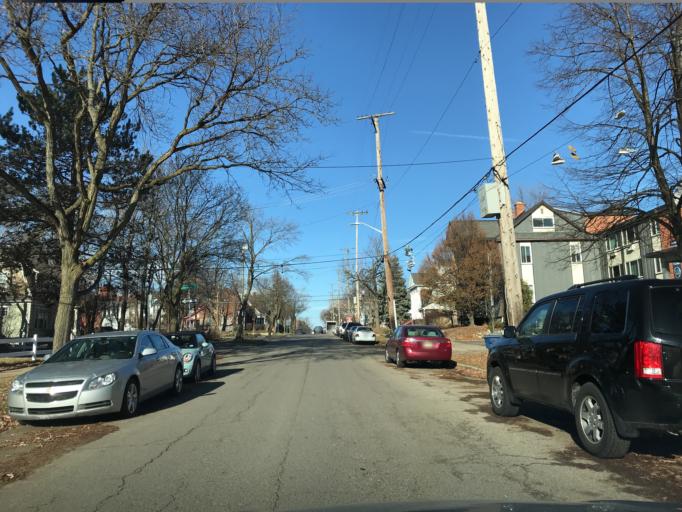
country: US
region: Michigan
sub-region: Washtenaw County
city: Ann Arbor
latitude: 42.2692
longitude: -83.7357
